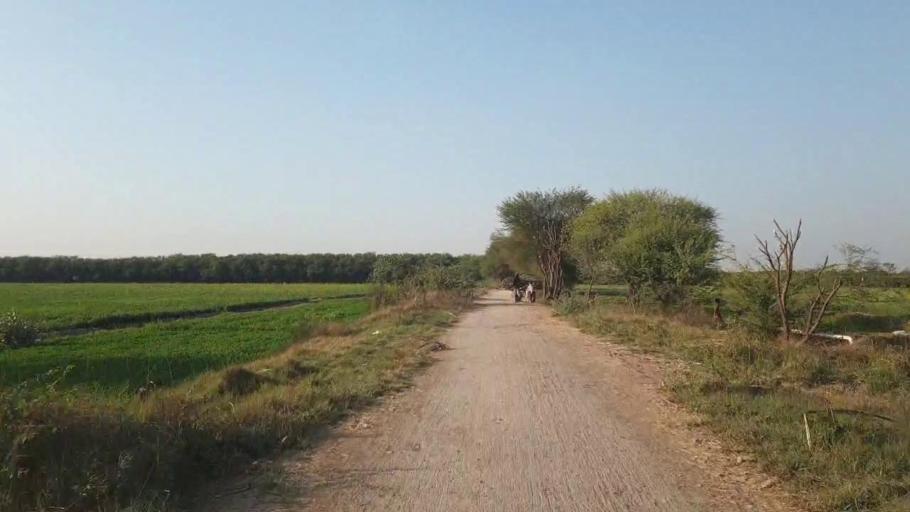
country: PK
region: Sindh
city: Mirpur Khas
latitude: 25.4338
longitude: 68.9108
